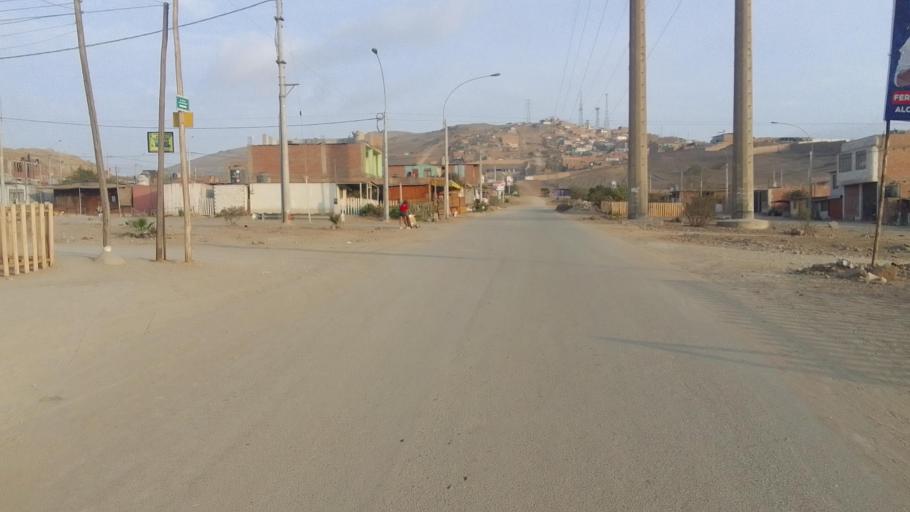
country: PE
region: Lima
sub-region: Lima
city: Santa Rosa
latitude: -11.8171
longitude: -77.1230
